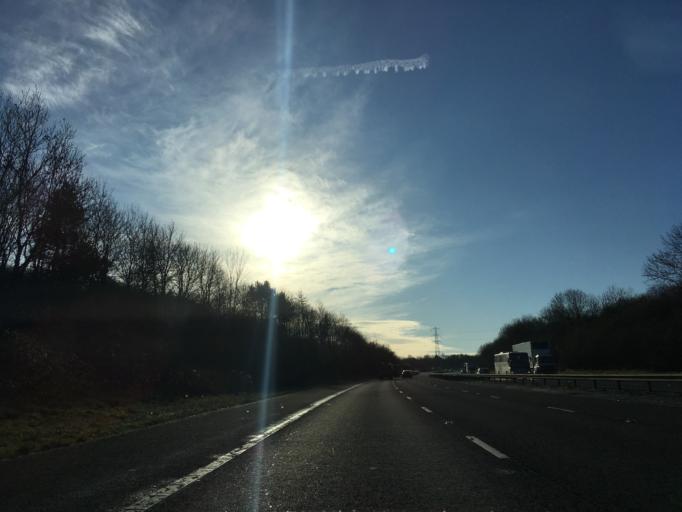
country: GB
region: England
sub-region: South Gloucestershire
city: Falfield
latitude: 51.6147
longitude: -2.4638
